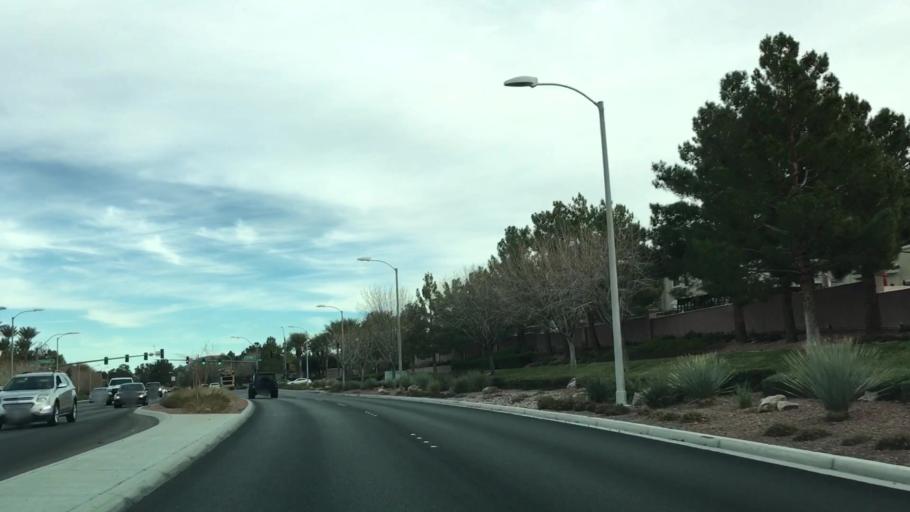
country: US
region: Nevada
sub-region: Clark County
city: Whitney
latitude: 36.0181
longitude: -115.0934
